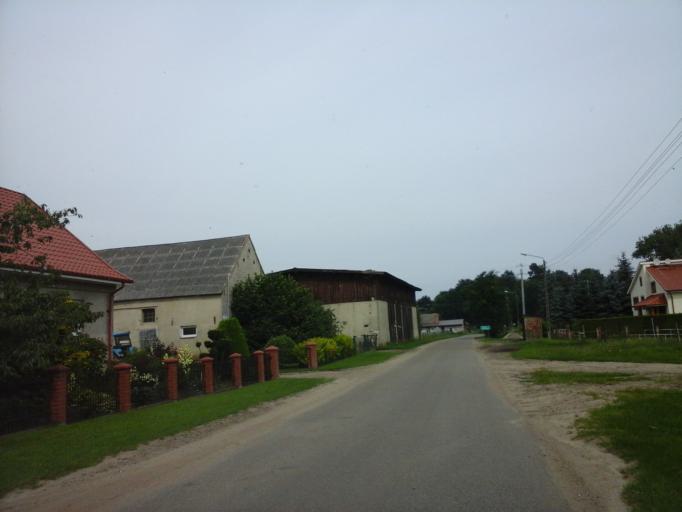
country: PL
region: West Pomeranian Voivodeship
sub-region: Powiat choszczenski
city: Bierzwnik
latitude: 53.0550
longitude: 15.5959
